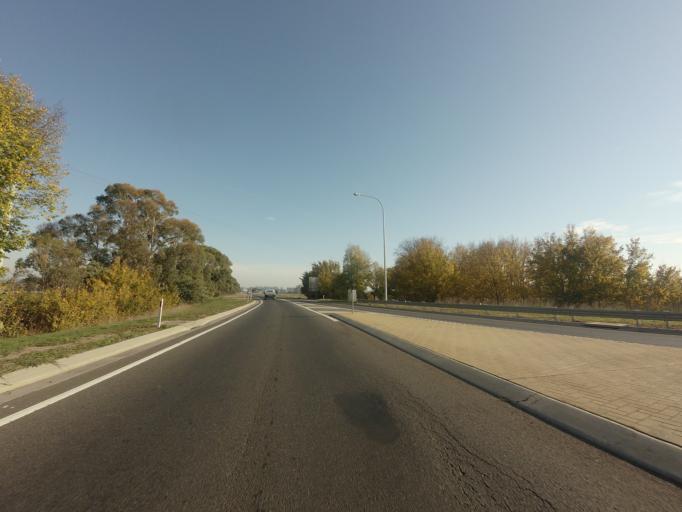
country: AU
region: Tasmania
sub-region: Northern Midlands
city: Longford
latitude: -41.5840
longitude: 147.1160
